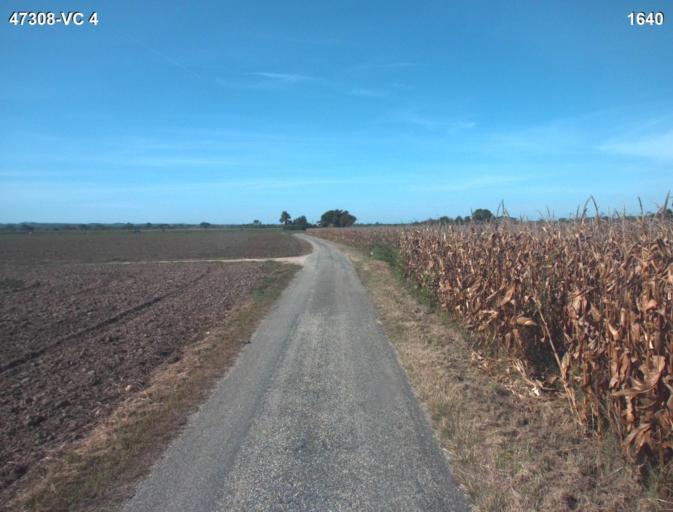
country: FR
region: Aquitaine
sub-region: Departement du Lot-et-Garonne
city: Buzet-sur-Baise
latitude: 44.2680
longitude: 0.3289
